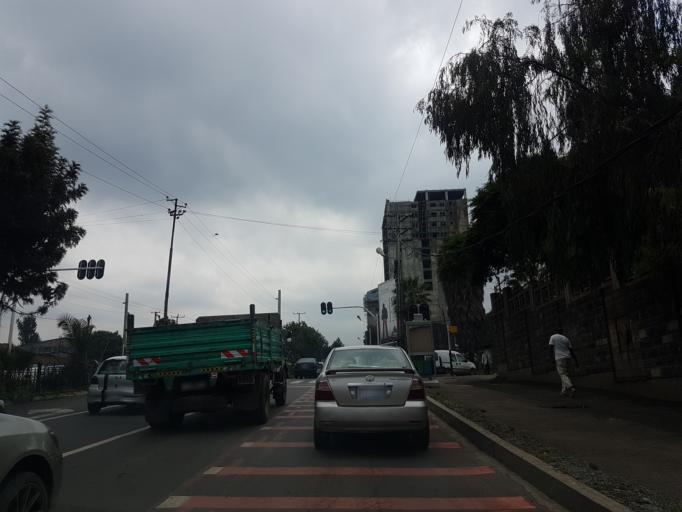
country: ET
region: Adis Abeba
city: Addis Ababa
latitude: 9.0023
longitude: 38.7411
